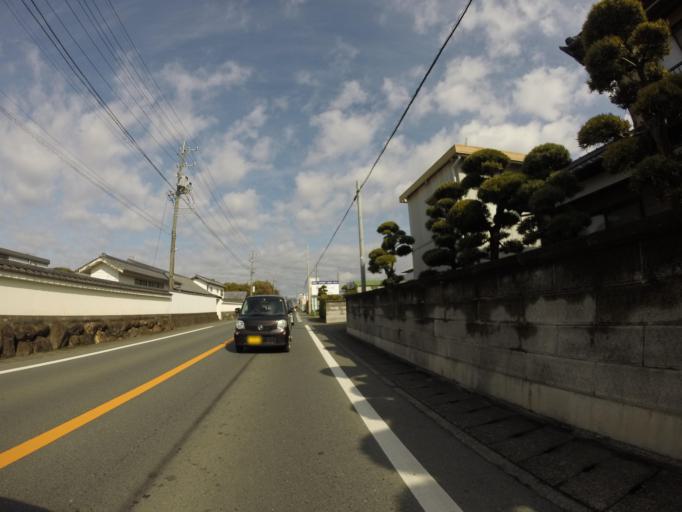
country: JP
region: Shizuoka
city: Hamakita
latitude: 34.7916
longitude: 137.7033
